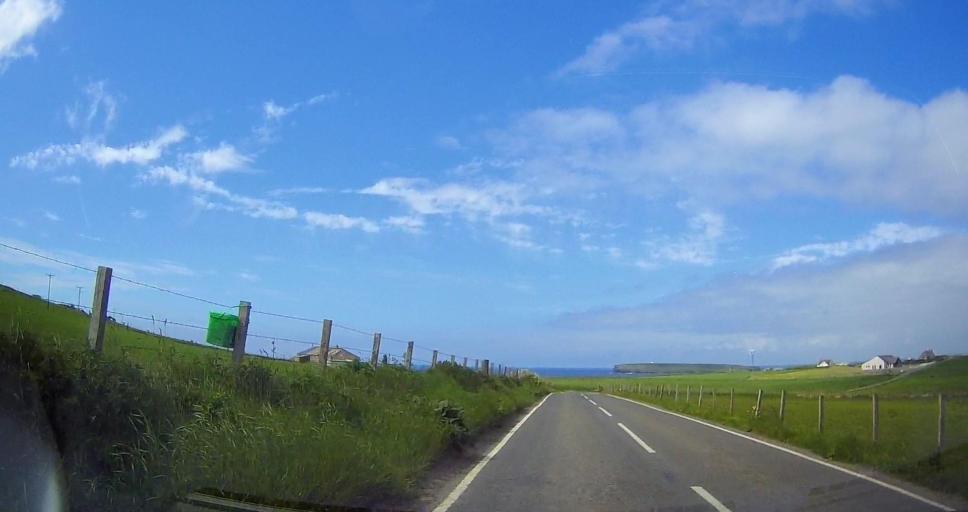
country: GB
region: Scotland
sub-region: Orkney Islands
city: Stromness
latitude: 59.1165
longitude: -3.3045
